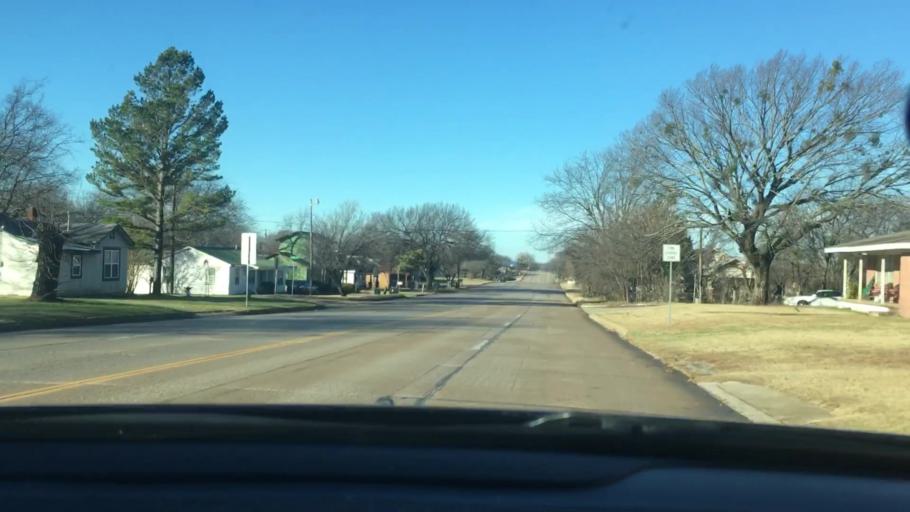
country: US
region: Oklahoma
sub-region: Murray County
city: Sulphur
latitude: 34.5109
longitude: -96.9557
